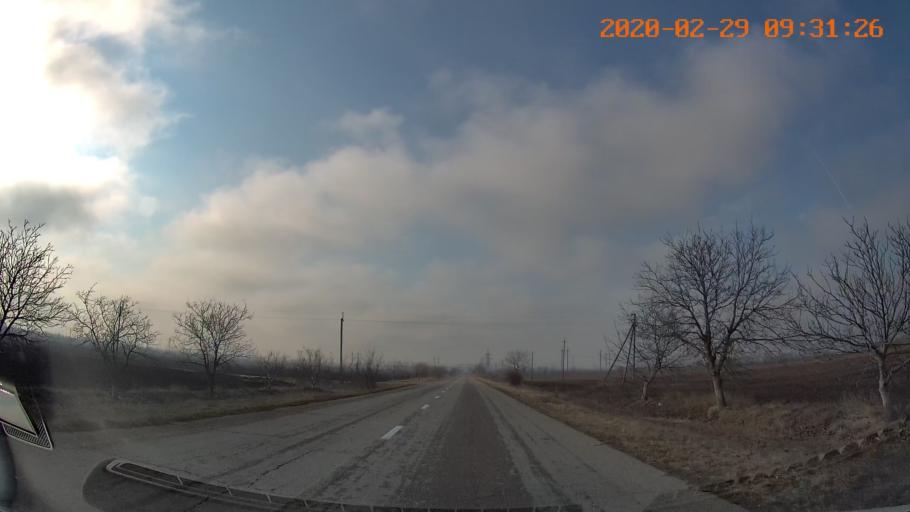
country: MD
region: Telenesti
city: Dnestrovsc
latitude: 46.6530
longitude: 29.9113
